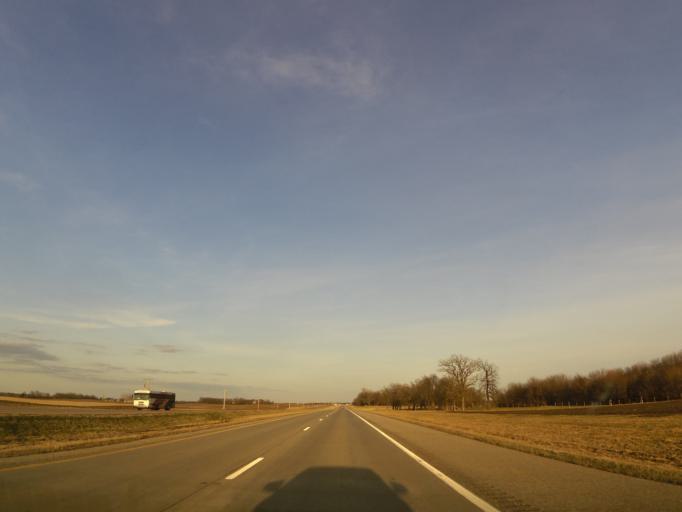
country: US
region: Minnesota
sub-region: Carver County
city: Norwood (historical)
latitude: 44.7679
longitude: -94.0087
